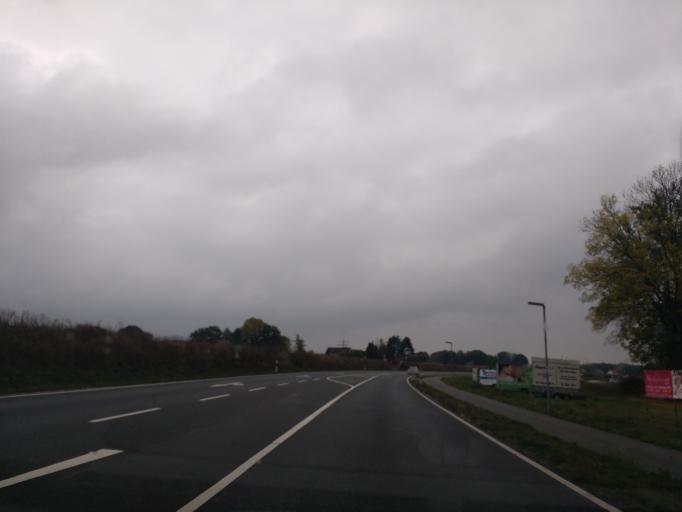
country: DE
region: North Rhine-Westphalia
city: Halle
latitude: 52.0315
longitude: 8.3768
